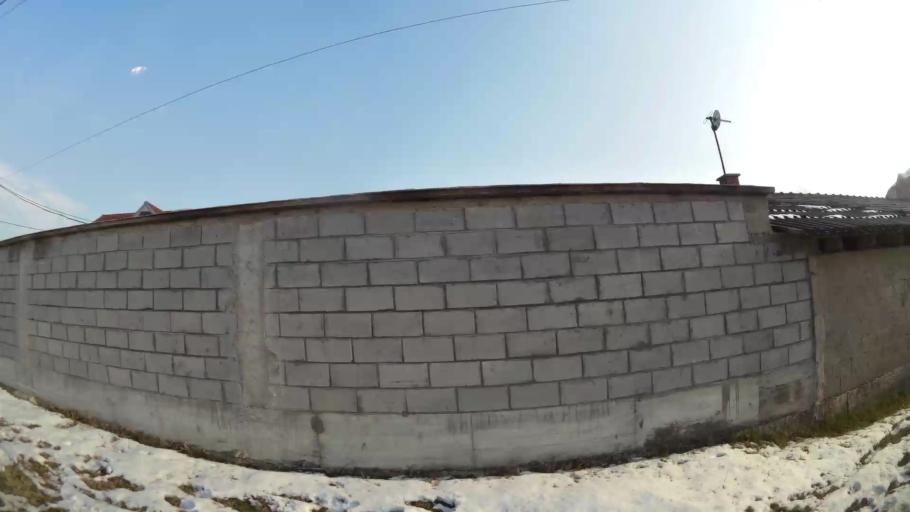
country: MK
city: Creshevo
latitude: 42.0180
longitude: 21.5084
